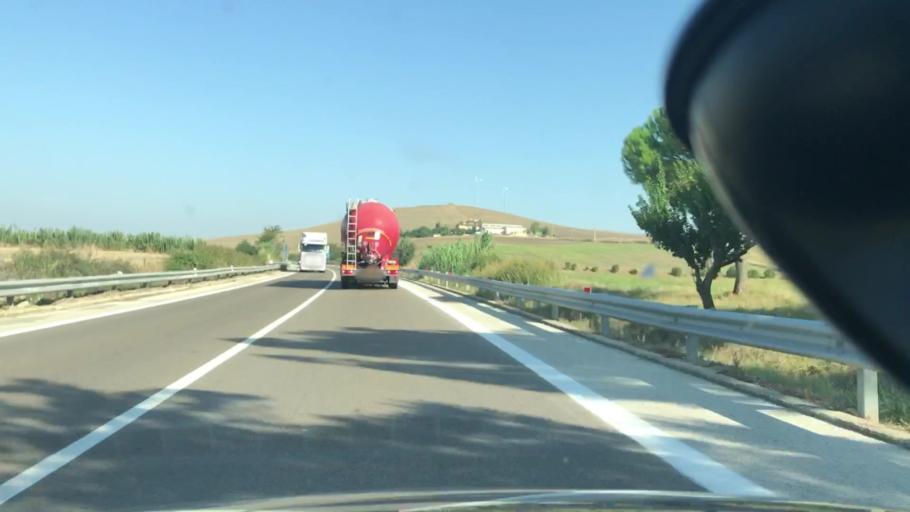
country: IT
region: Basilicate
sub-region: Provincia di Matera
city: Irsina
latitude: 40.8070
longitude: 16.2726
